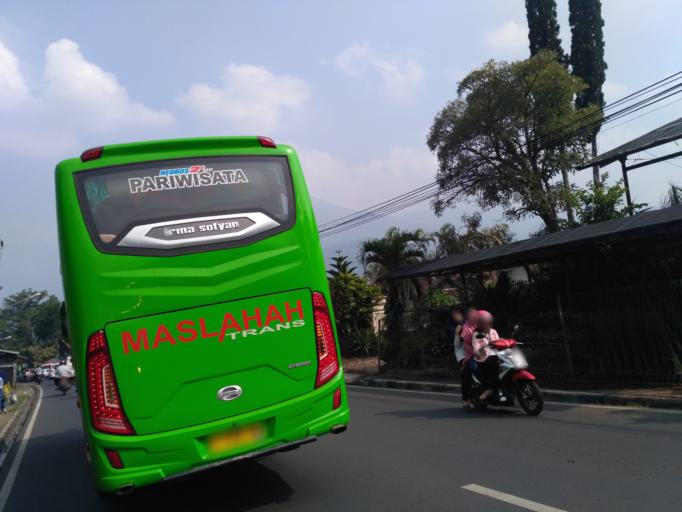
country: ID
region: East Java
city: Batu
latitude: -7.8561
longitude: 112.5270
